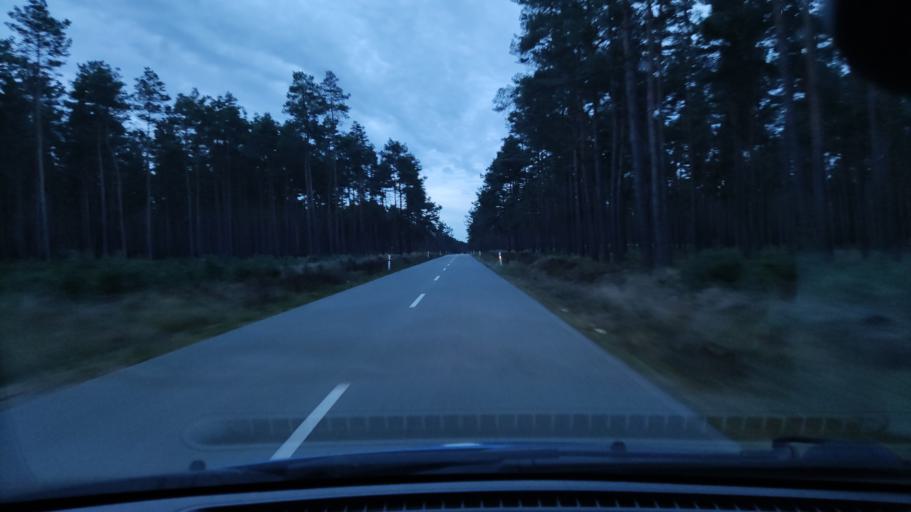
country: DE
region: Lower Saxony
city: Prezelle
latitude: 52.9899
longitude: 11.3958
